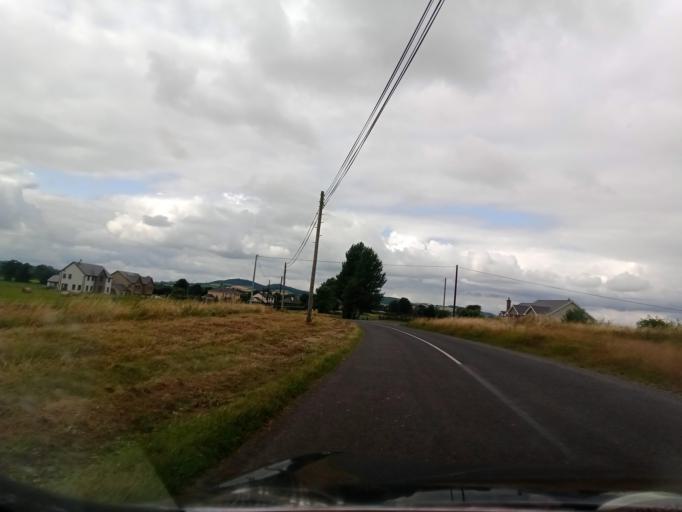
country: IE
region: Leinster
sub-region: Laois
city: Stradbally
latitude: 52.9770
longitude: -7.1797
